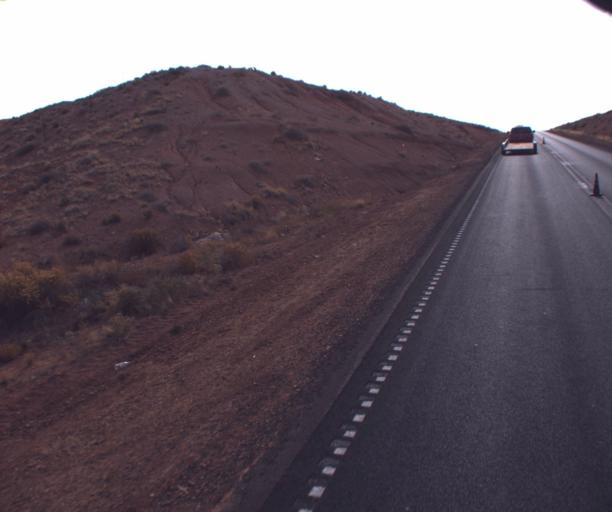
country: US
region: Arizona
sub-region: Apache County
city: Chinle
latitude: 36.1052
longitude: -109.6319
